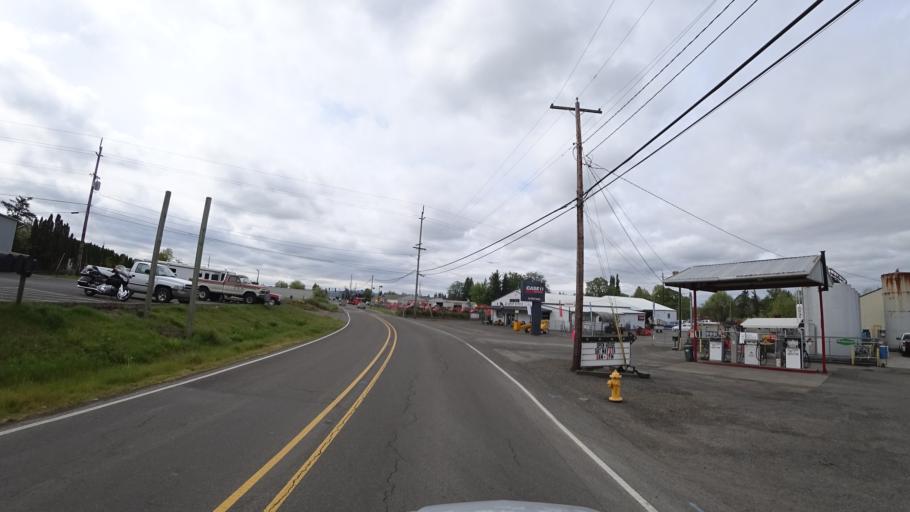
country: US
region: Oregon
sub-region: Washington County
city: Hillsboro
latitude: 45.5218
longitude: -123.0021
